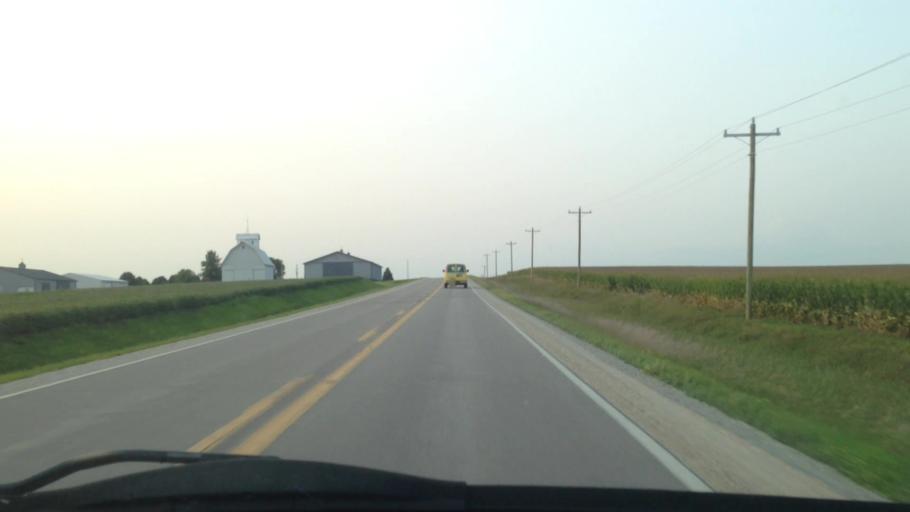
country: US
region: Iowa
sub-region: Benton County
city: Atkins
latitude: 42.0414
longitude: -91.8694
